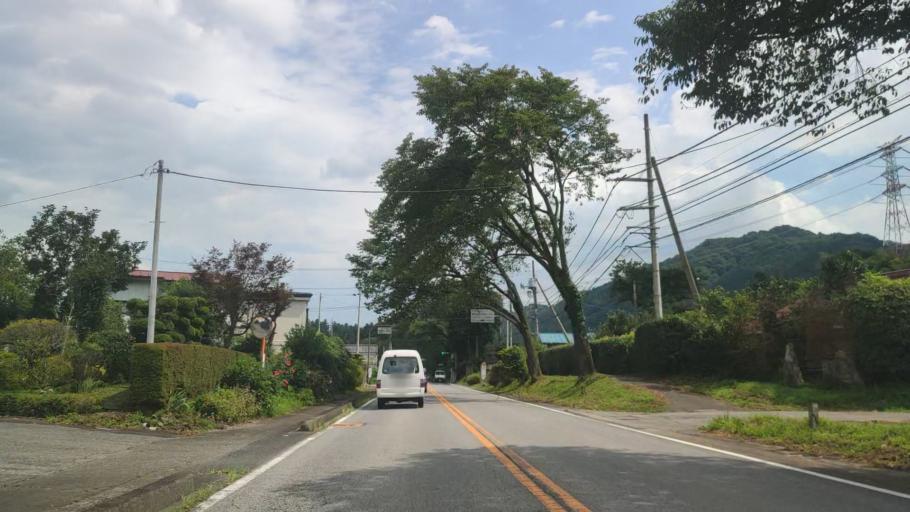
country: JP
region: Tochigi
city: Utsunomiya-shi
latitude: 36.6720
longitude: 139.8097
